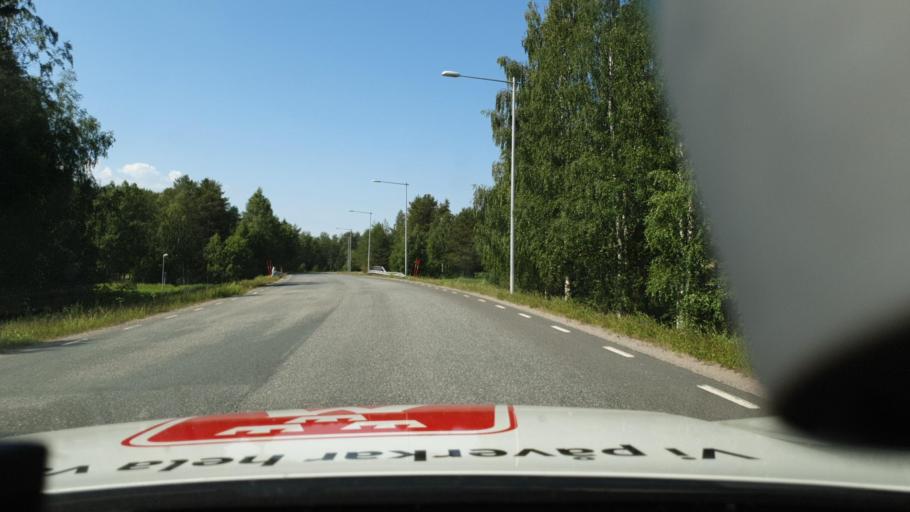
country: SE
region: Norrbotten
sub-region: Kalix Kommun
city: Rolfs
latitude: 65.8676
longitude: 23.1259
